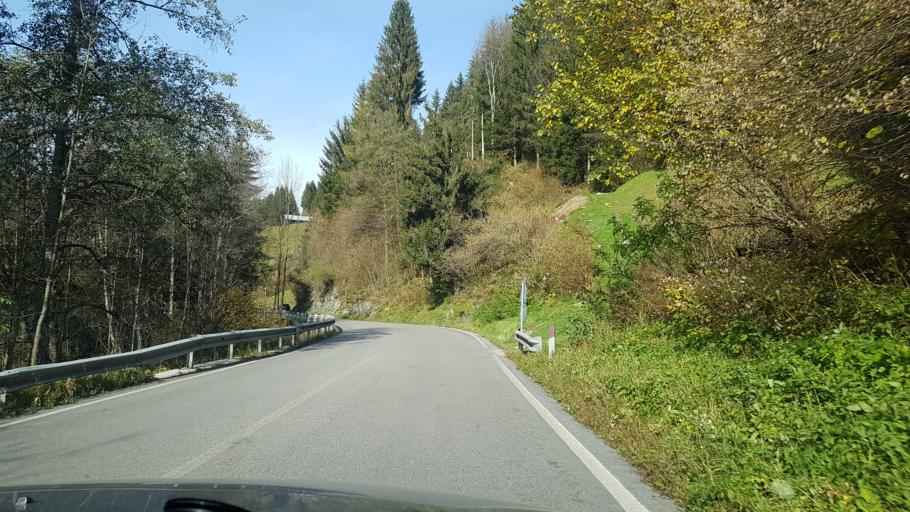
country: IT
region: Veneto
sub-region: Provincia di Belluno
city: Santo Stefano di Cadore
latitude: 46.5662
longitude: 12.5432
